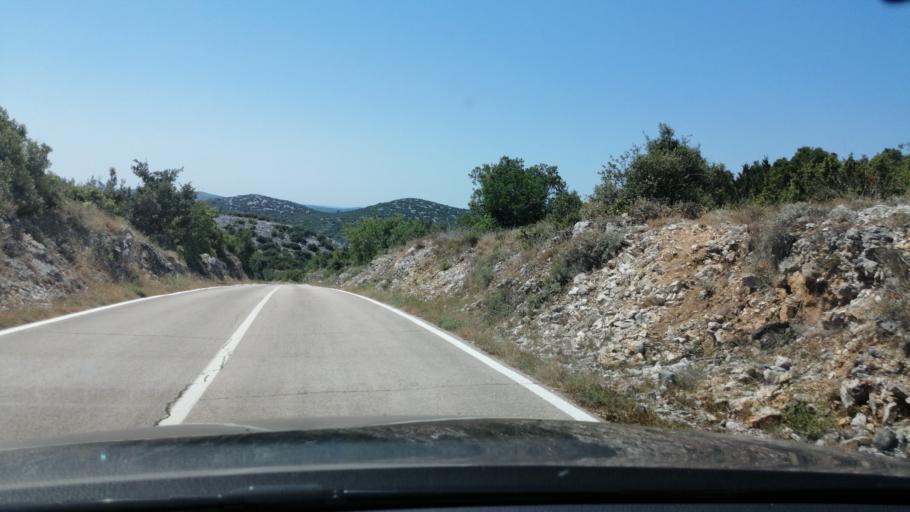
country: HR
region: Sibensko-Kniniska
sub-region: Grad Sibenik
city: Pirovac
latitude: 43.8563
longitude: 15.6915
